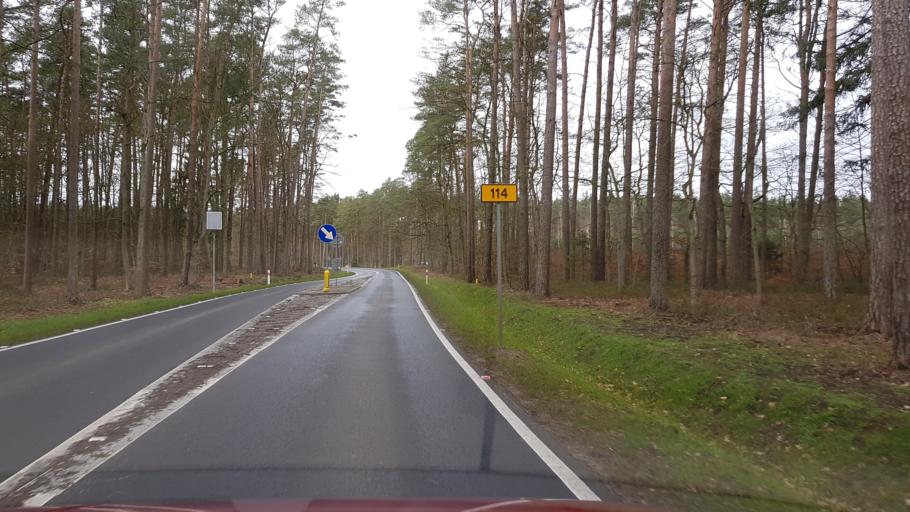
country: PL
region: West Pomeranian Voivodeship
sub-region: Powiat policki
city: Police
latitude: 53.6540
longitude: 14.4800
